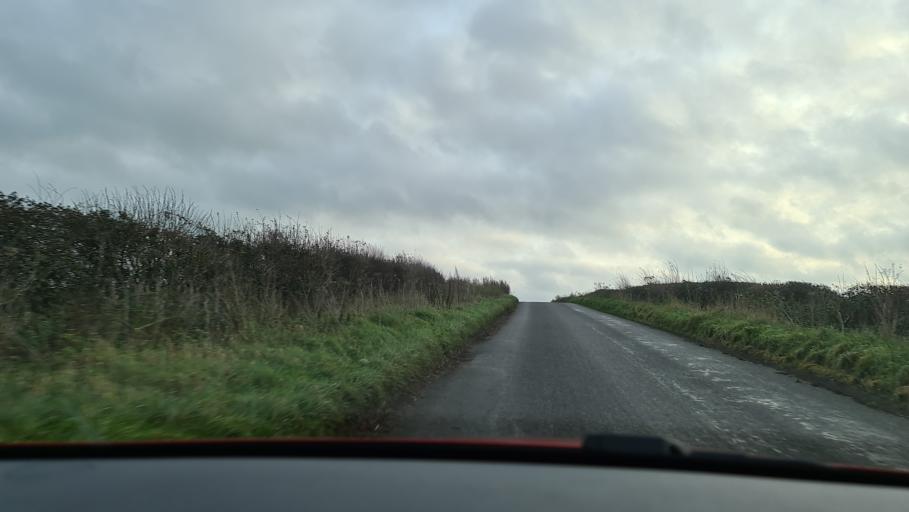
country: GB
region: England
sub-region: Buckinghamshire
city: Long Crendon
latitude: 51.7975
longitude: -0.9746
